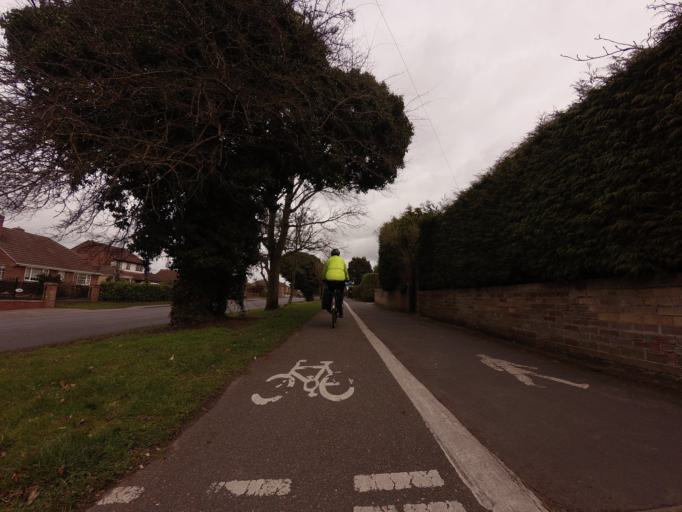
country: GB
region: England
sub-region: Lincolnshire
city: Grantham
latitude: 52.9218
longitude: -0.6323
